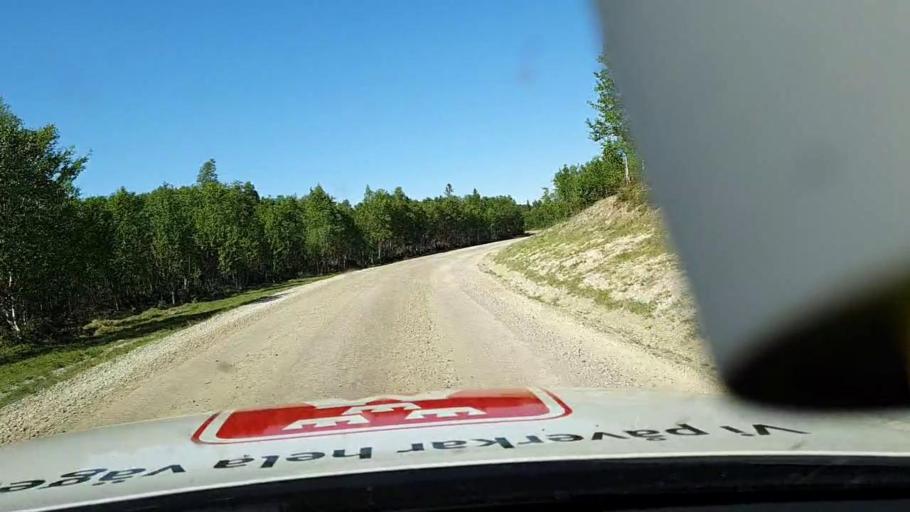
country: SE
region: Jaemtland
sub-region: Are Kommun
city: Are
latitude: 62.6077
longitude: 12.6216
